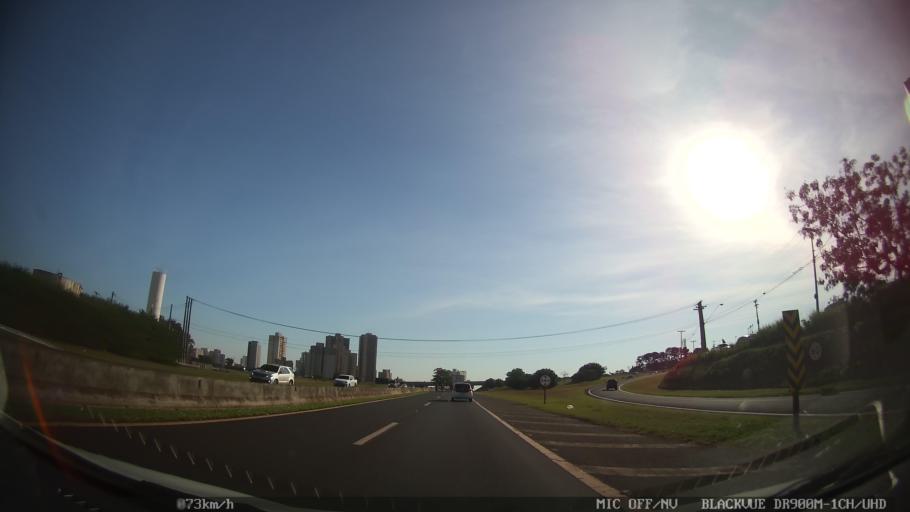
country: BR
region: Sao Paulo
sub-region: Ribeirao Preto
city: Ribeirao Preto
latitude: -21.2260
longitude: -47.8173
